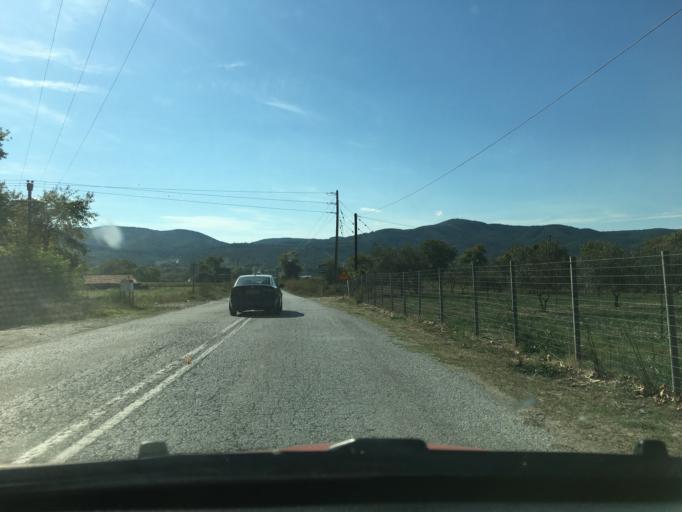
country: GR
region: Central Macedonia
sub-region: Nomos Chalkidikis
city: Ierissos
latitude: 40.3957
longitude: 23.7904
